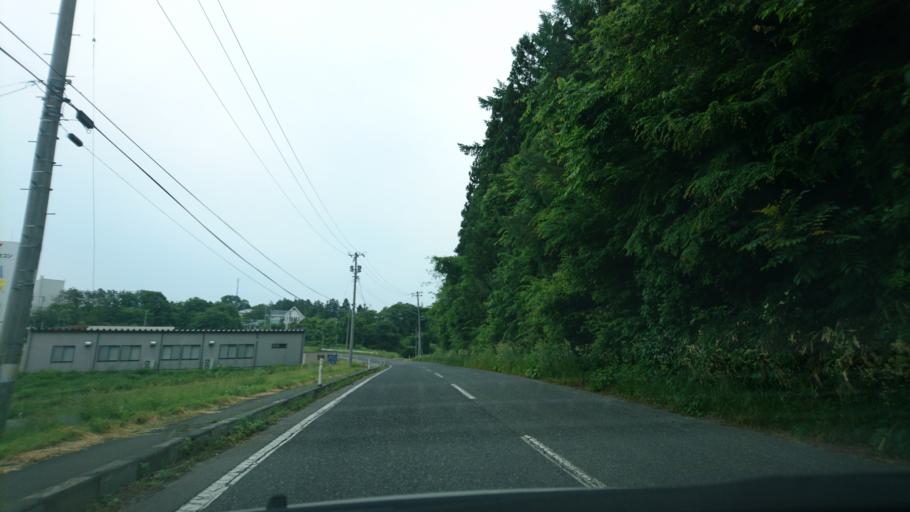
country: JP
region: Iwate
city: Ichinoseki
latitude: 38.8841
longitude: 141.1364
